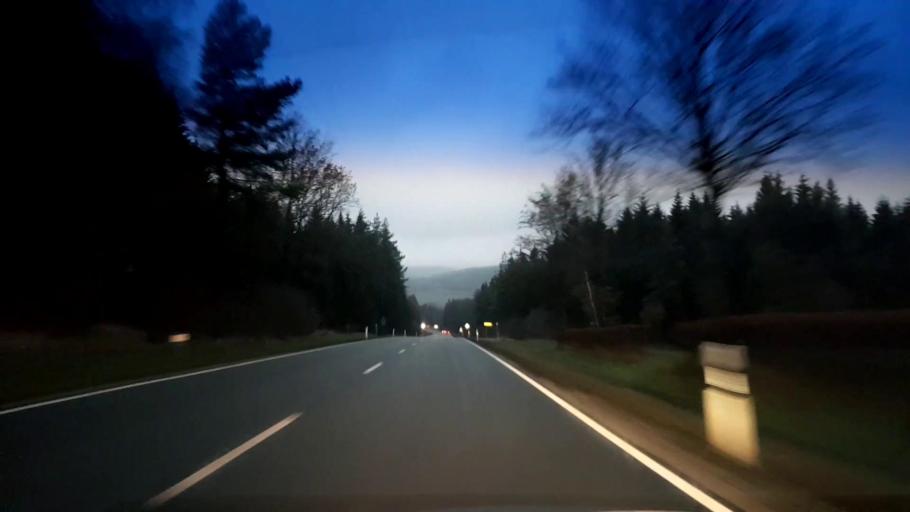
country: DE
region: Bavaria
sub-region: Upper Palatinate
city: Erbendorf
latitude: 49.8411
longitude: 12.0059
